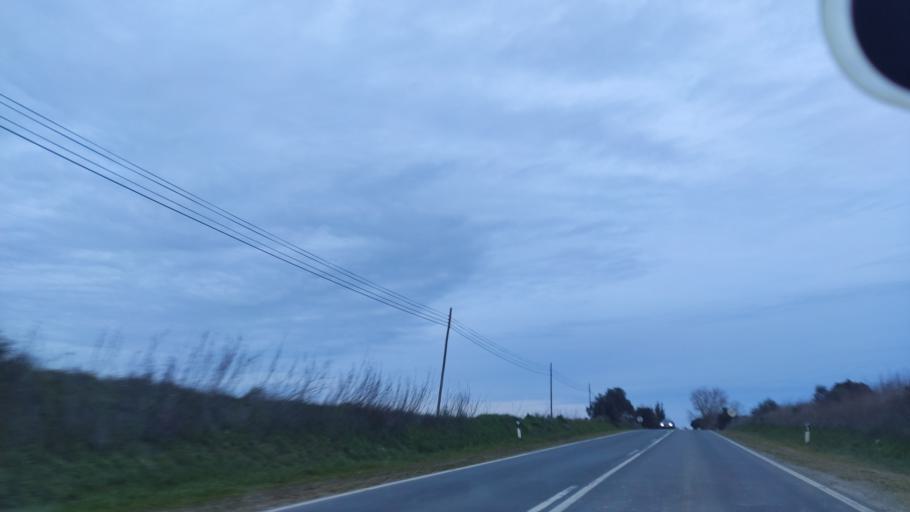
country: PT
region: Beja
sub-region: Beja
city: Ferreira do Alentejo
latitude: 38.0556
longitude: -7.9948
